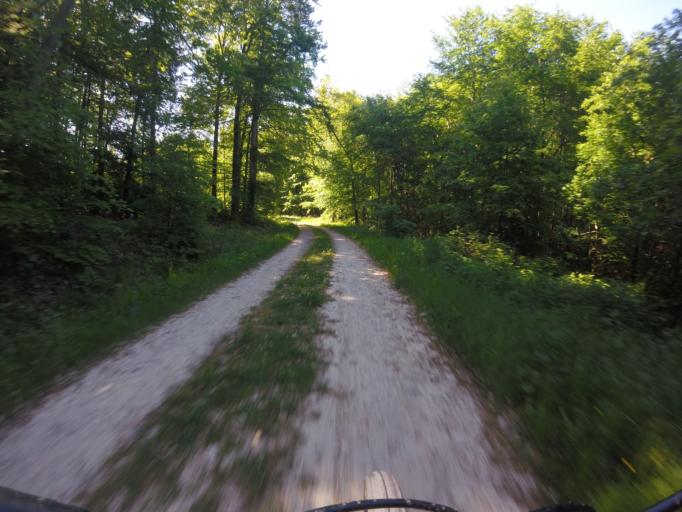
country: DE
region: Baden-Wuerttemberg
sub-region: Regierungsbezirk Stuttgart
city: Aspach
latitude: 49.0072
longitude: 9.4088
